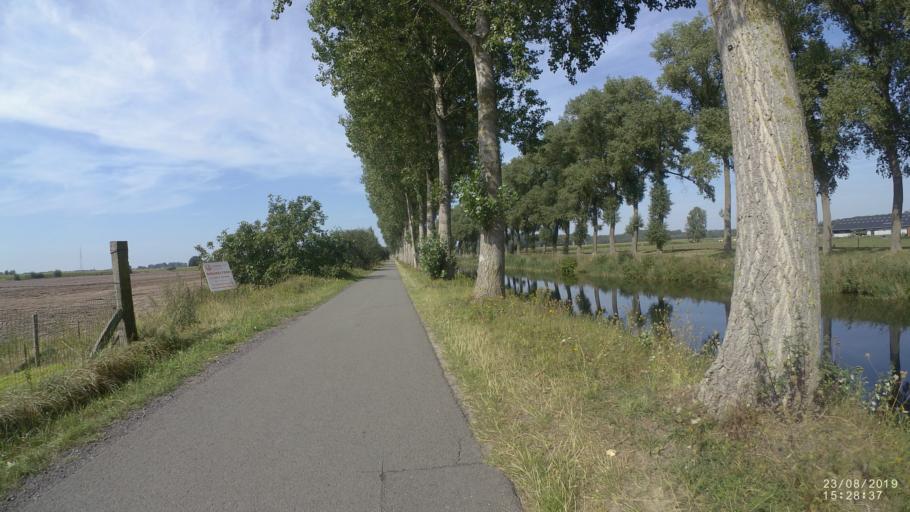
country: BE
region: Flanders
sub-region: Provincie Oost-Vlaanderen
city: Zomergem
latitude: 51.1427
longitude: 3.5566
